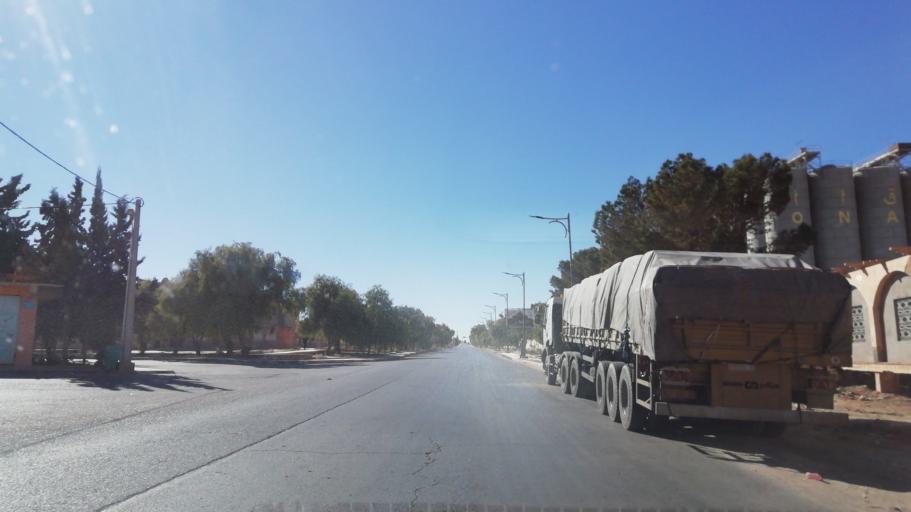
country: DZ
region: Saida
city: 'Ain el Hadjar
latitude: 34.0430
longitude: 0.0836
